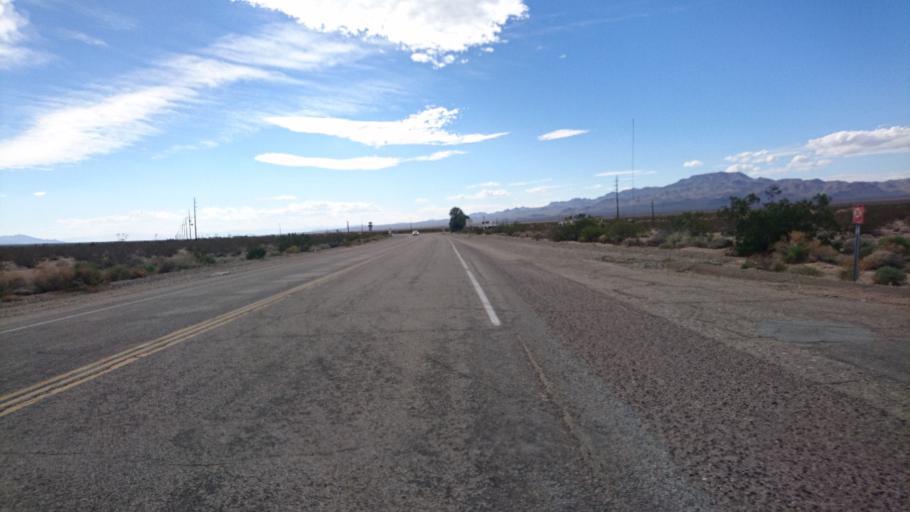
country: US
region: California
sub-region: San Bernardino County
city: Needles
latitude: 34.7525
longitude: -115.2249
